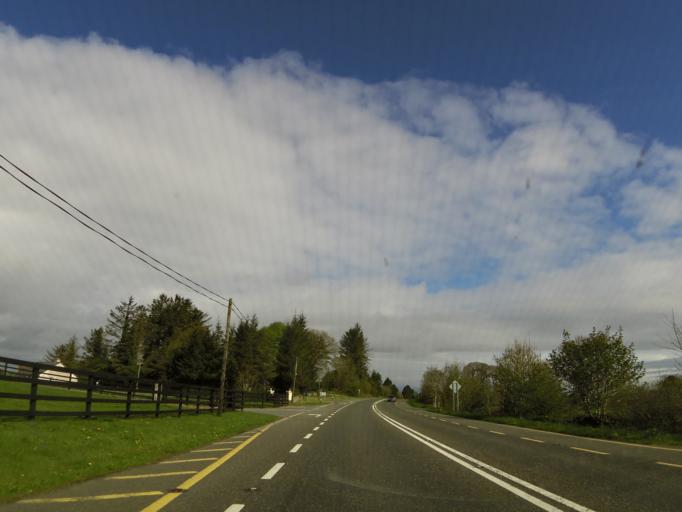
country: IE
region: Connaught
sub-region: Sligo
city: Tobercurry
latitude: 53.9276
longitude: -8.7843
